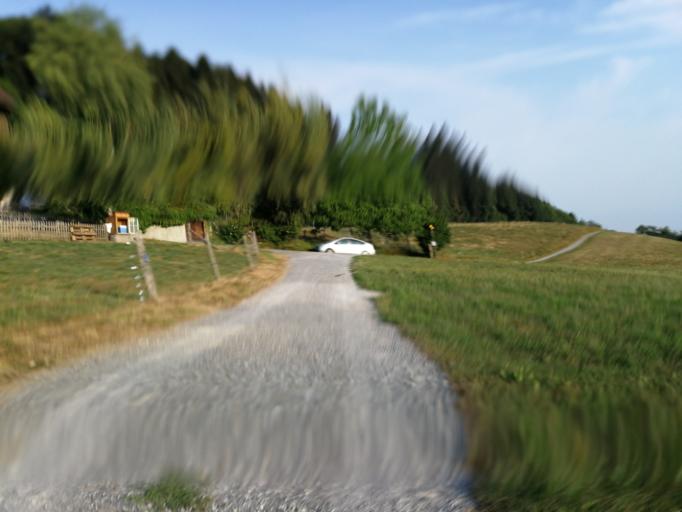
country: CH
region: Zurich
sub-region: Bezirk Uster
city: Esslingen
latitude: 47.2771
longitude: 8.7138
